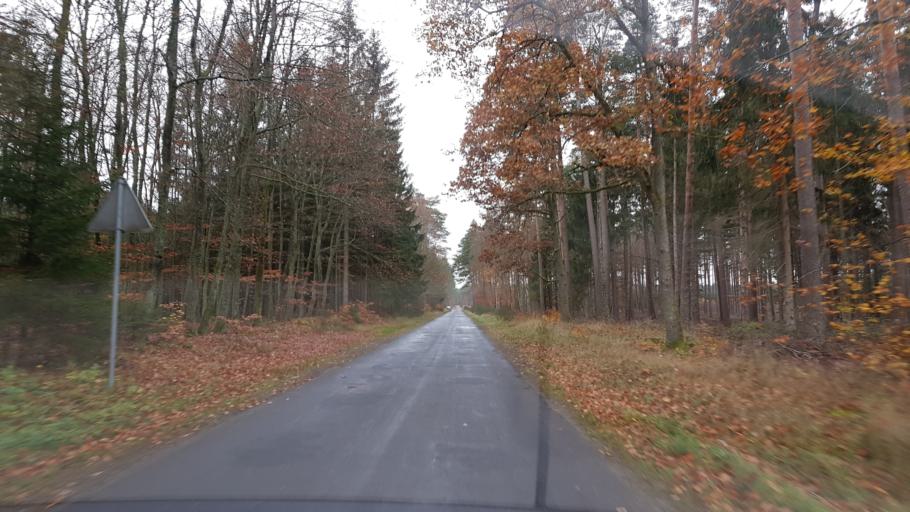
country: PL
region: West Pomeranian Voivodeship
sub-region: Powiat koszalinski
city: Bobolice
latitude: 54.0740
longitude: 16.5741
